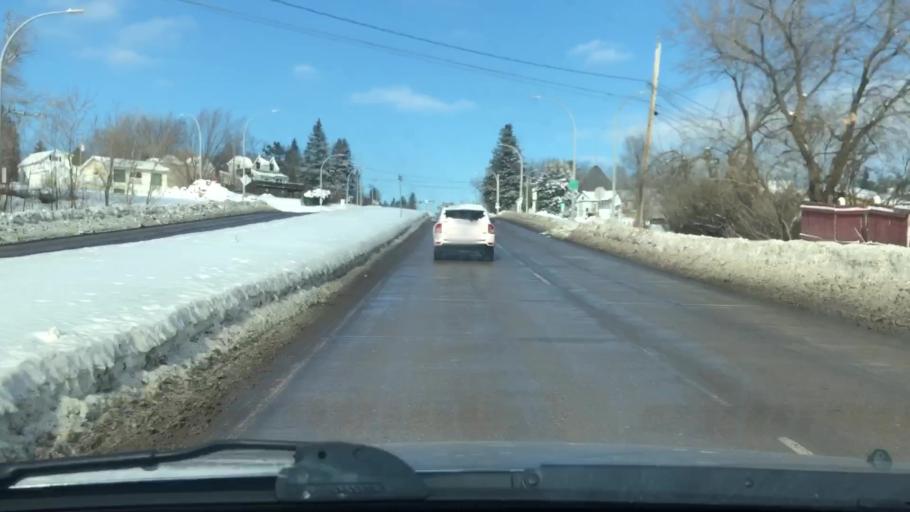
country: US
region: Minnesota
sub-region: Saint Louis County
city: Duluth
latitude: 46.7928
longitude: -92.1070
